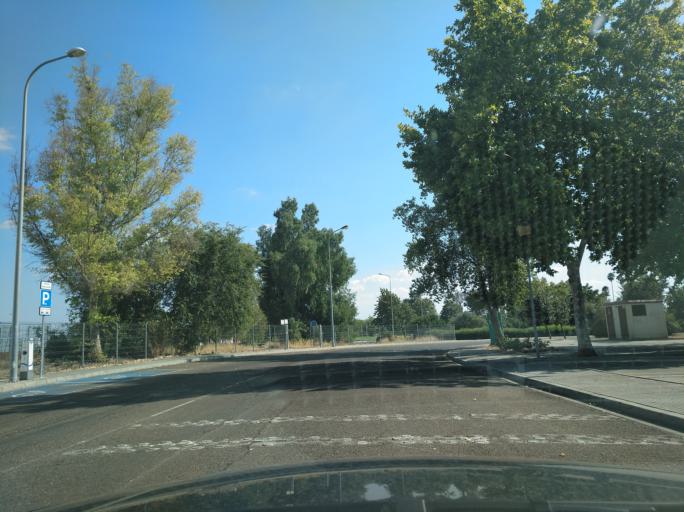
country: ES
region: Extremadura
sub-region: Provincia de Badajoz
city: Badajoz
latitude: 38.8837
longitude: -7.0030
